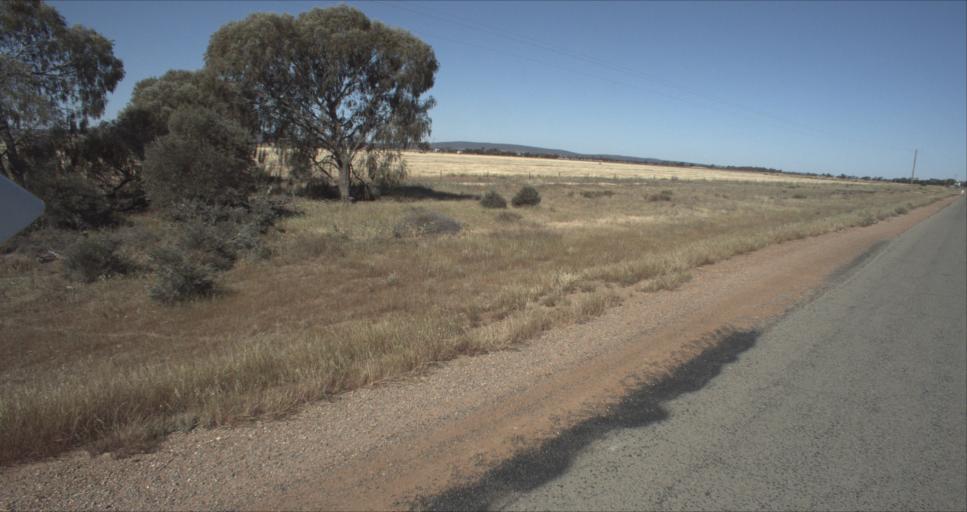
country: AU
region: New South Wales
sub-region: Leeton
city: Leeton
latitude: -34.4887
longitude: 146.3805
